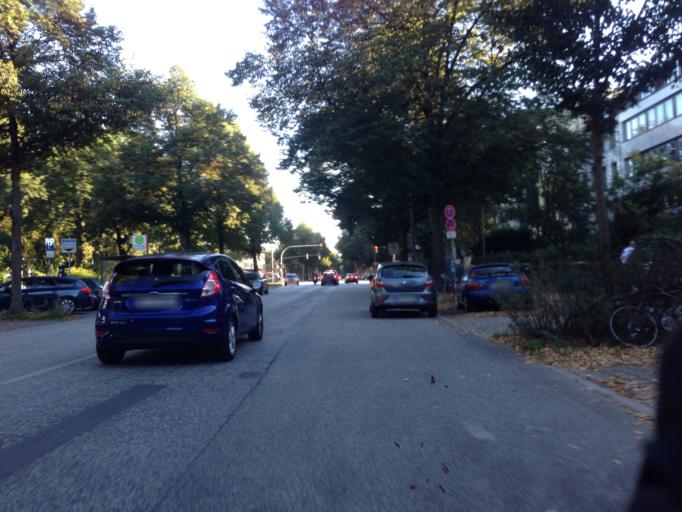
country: DE
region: Hamburg
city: Eimsbuettel
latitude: 53.5738
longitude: 9.9887
